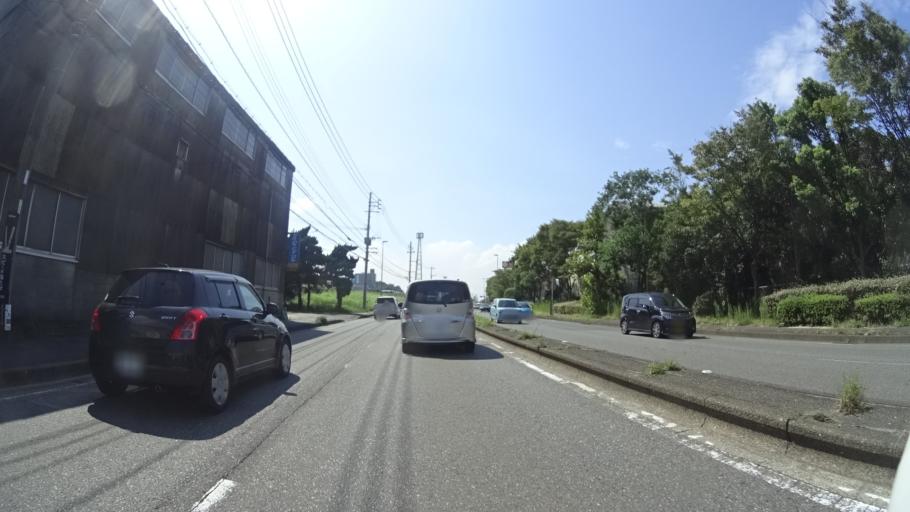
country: JP
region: Yamaguchi
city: Shimonoseki
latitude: 33.8935
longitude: 130.9145
